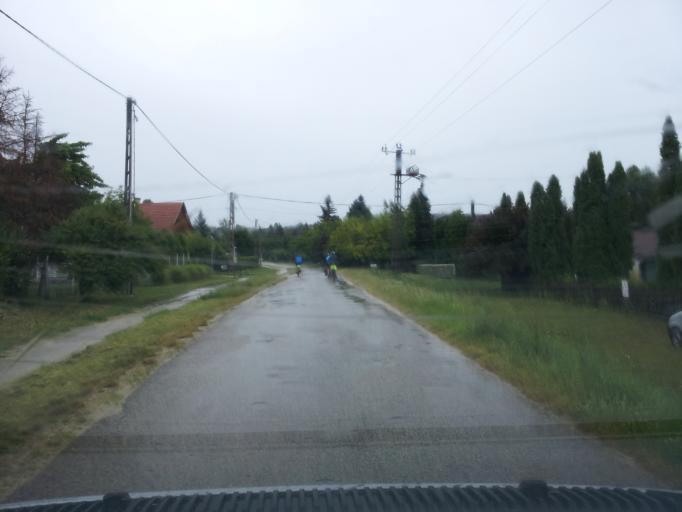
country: HU
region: Veszprem
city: Balatonkenese
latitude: 47.0294
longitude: 18.1305
